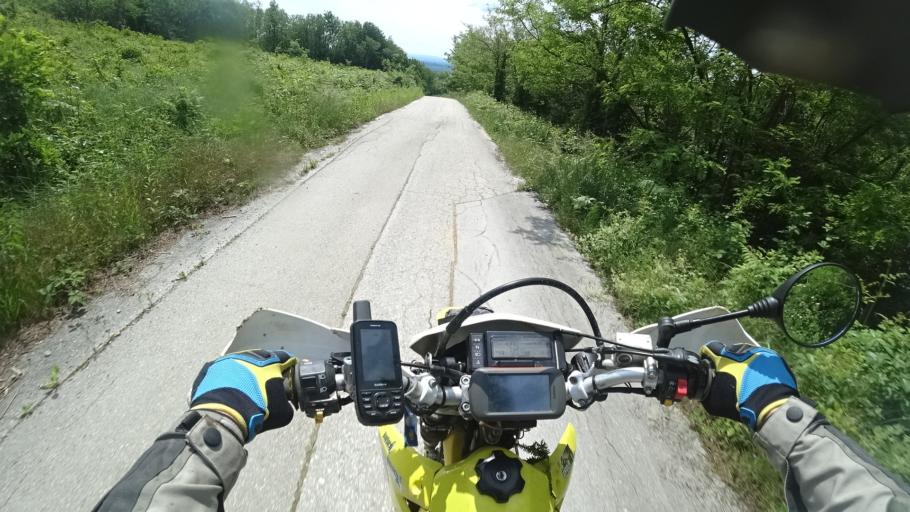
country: HR
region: Sisacko-Moslavacka
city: Gvozd
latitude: 45.3930
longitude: 15.8559
